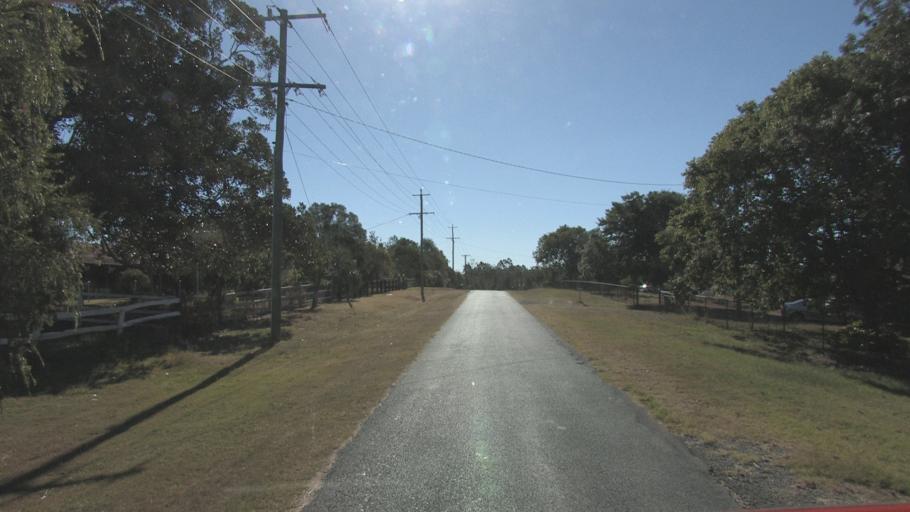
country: AU
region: Queensland
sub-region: Logan
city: North Maclean
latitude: -27.7840
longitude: 153.0195
